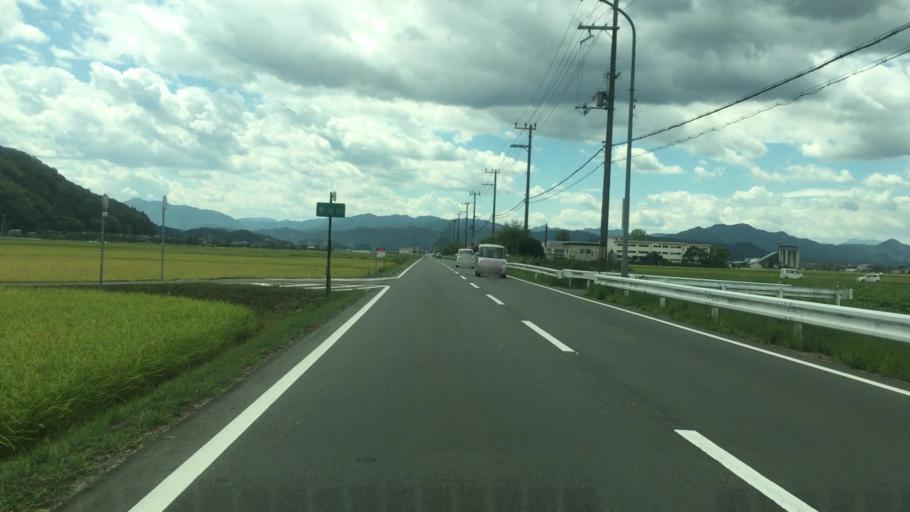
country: JP
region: Hyogo
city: Toyooka
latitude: 35.5353
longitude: 134.8397
